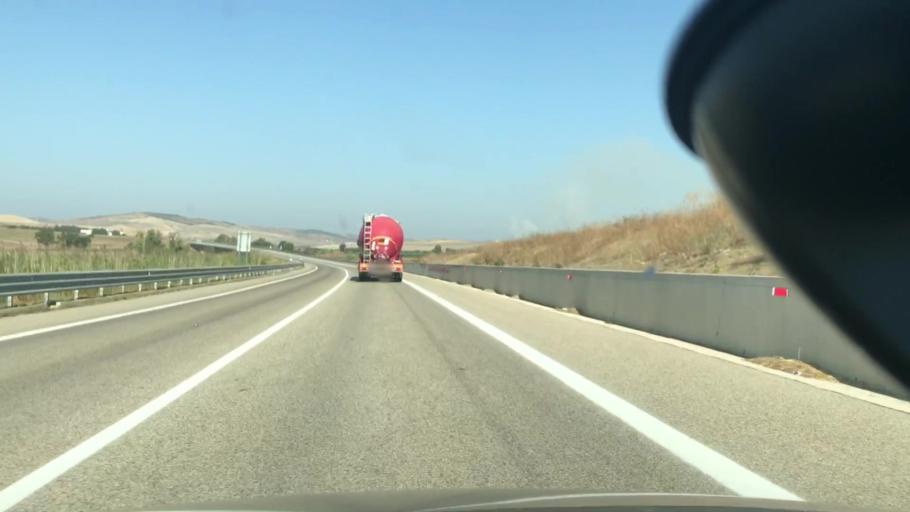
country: IT
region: Basilicate
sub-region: Provincia di Matera
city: Irsina
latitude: 40.7799
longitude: 16.3157
